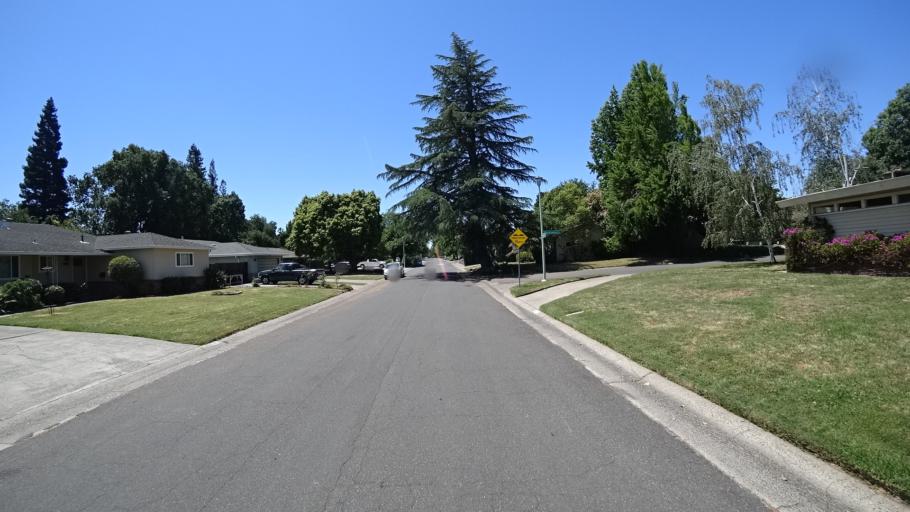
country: US
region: California
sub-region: Sacramento County
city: Sacramento
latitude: 38.5340
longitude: -121.5101
